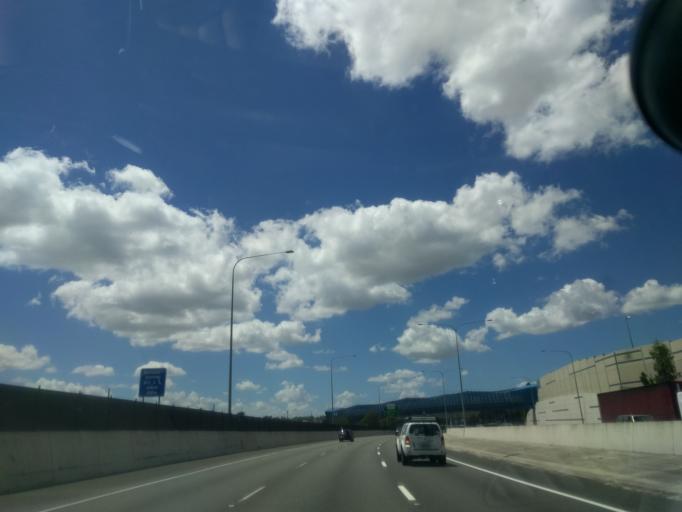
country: AU
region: Queensland
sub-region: Ipswich
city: Goodna
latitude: -27.6048
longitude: 152.8935
